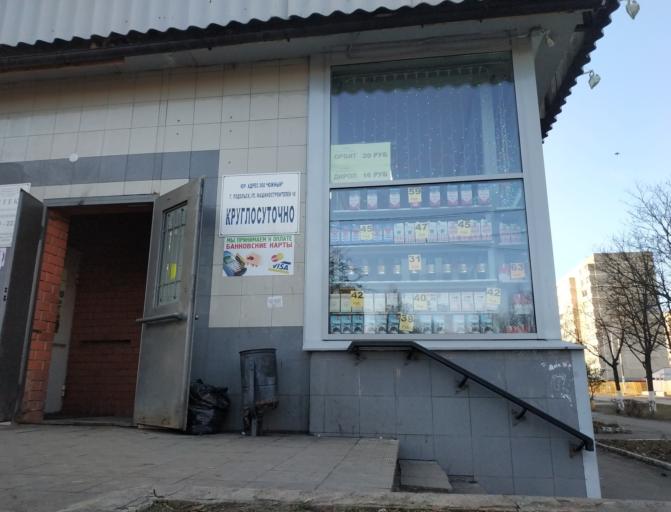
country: RU
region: Moskovskaya
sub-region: Podol'skiy Rayon
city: Podol'sk
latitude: 55.4094
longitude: 37.5706
